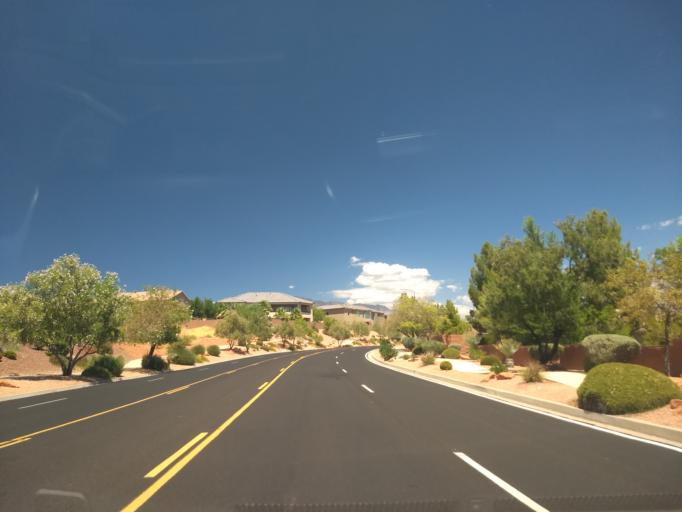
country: US
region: Utah
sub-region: Washington County
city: Washington
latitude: 37.1495
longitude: -113.5293
